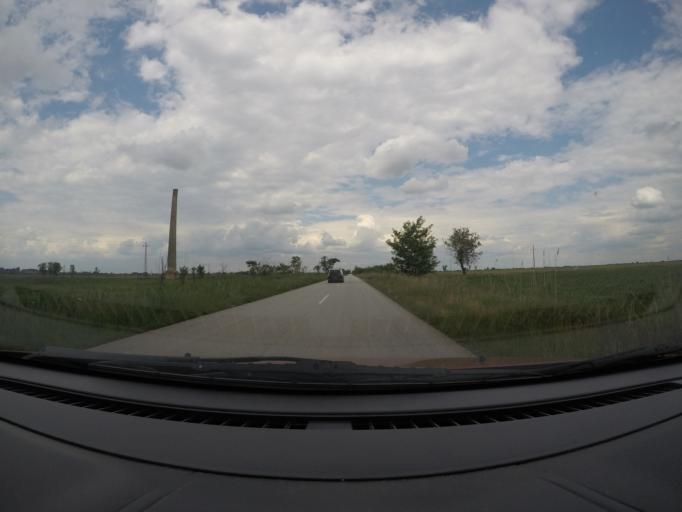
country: RS
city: Begejci
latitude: 45.4907
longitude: 20.5826
